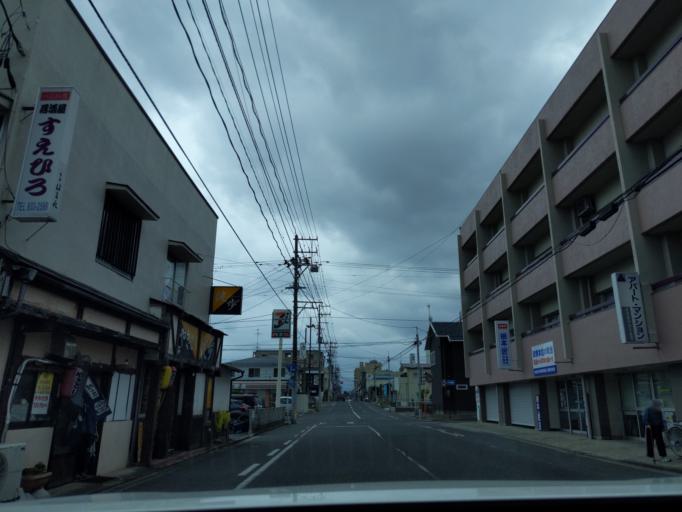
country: JP
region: Fukushima
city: Koriyama
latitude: 37.4040
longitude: 140.3774
